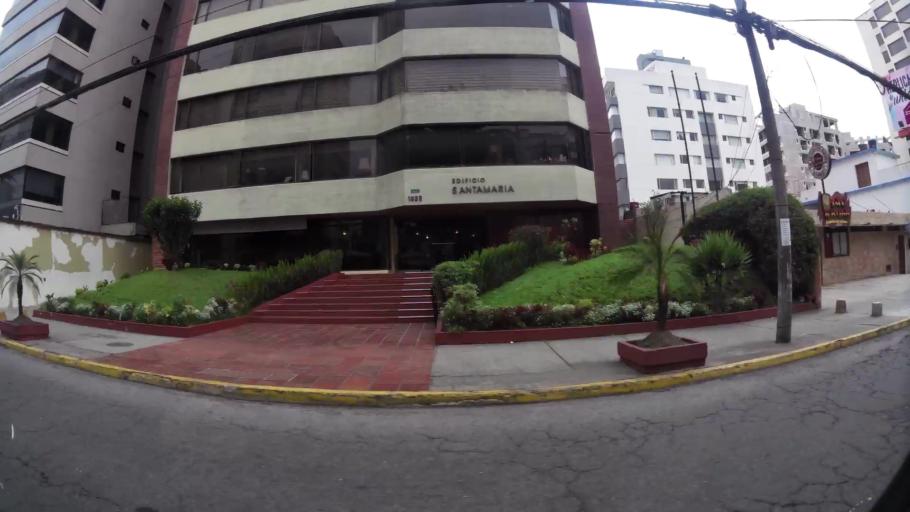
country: EC
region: Pichincha
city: Quito
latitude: -0.1939
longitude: -78.4831
